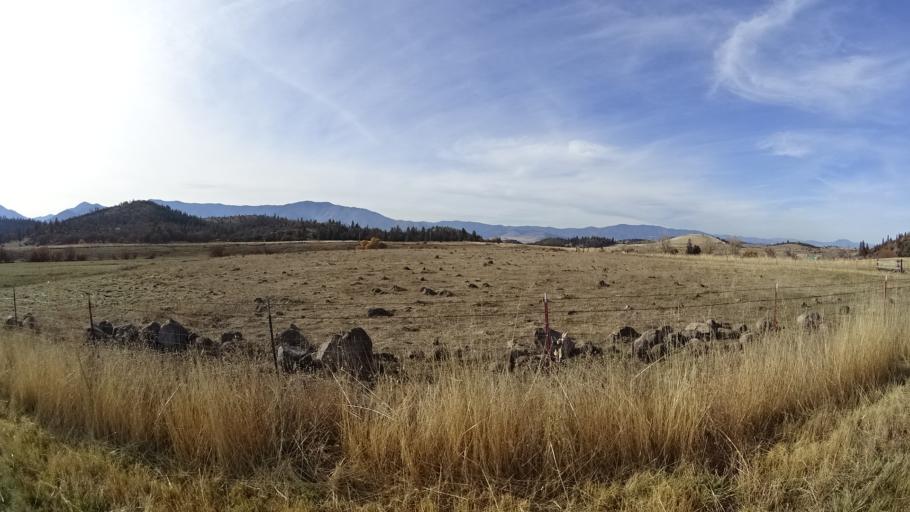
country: US
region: California
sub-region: Siskiyou County
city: Weed
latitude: 41.4609
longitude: -122.3838
